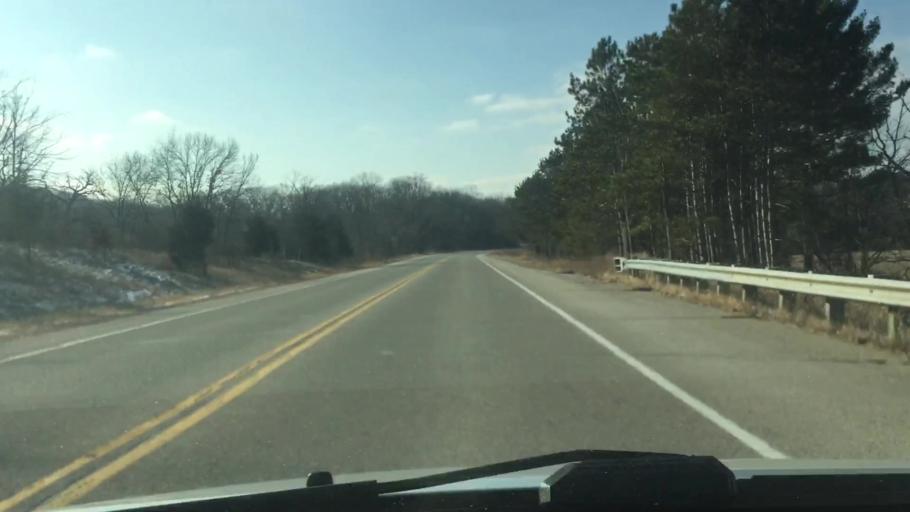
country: US
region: Wisconsin
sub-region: Waukesha County
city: Eagle
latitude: 42.8806
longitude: -88.4946
